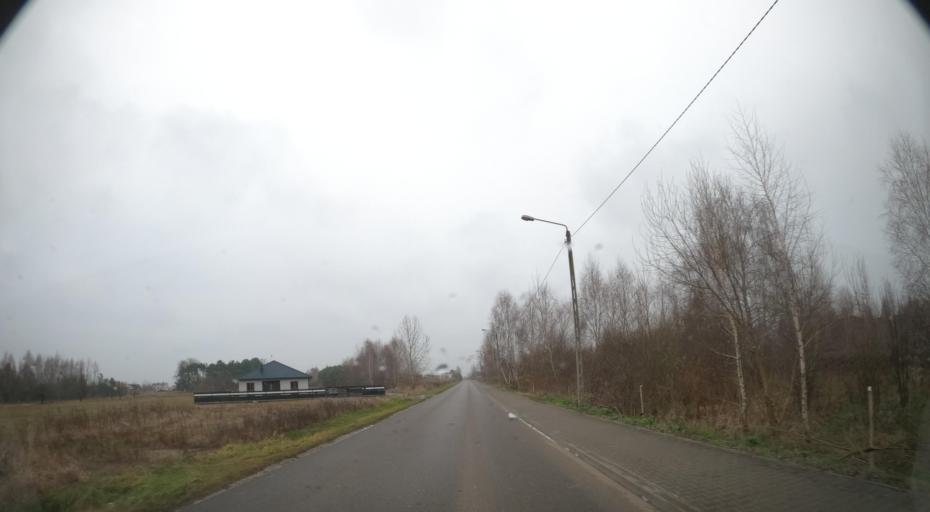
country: PL
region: Masovian Voivodeship
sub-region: Powiat radomski
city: Skaryszew
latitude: 51.3899
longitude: 21.2613
